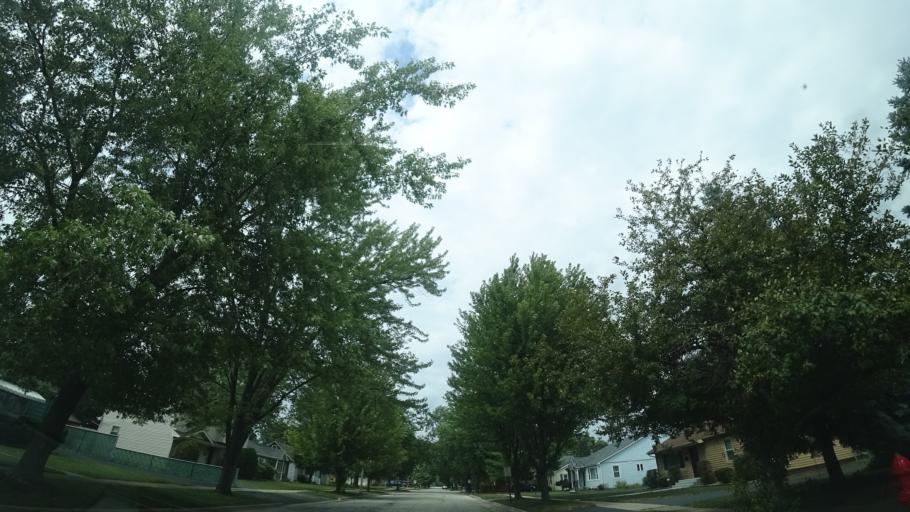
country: US
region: Illinois
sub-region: Cook County
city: Chicago Ridge
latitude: 41.6912
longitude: -87.7776
